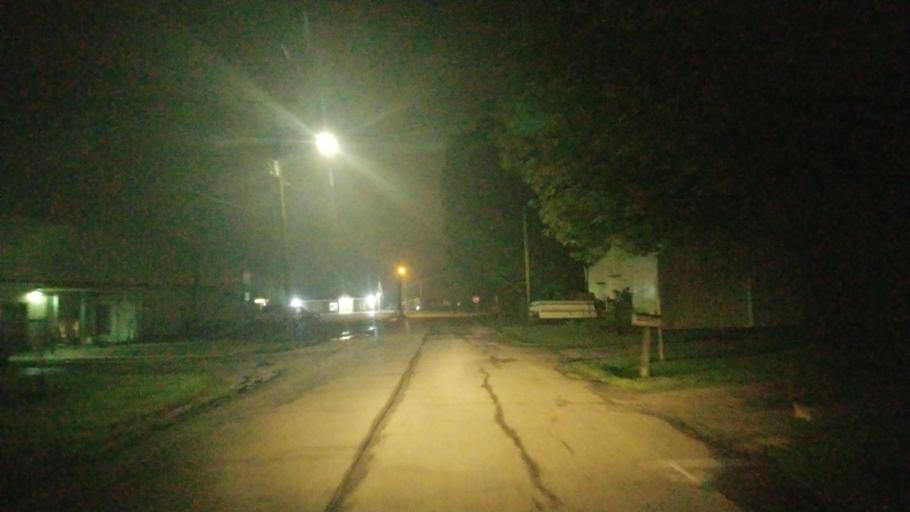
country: US
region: Missouri
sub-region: Pike County
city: Bowling Green
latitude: 39.3412
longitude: -91.2015
